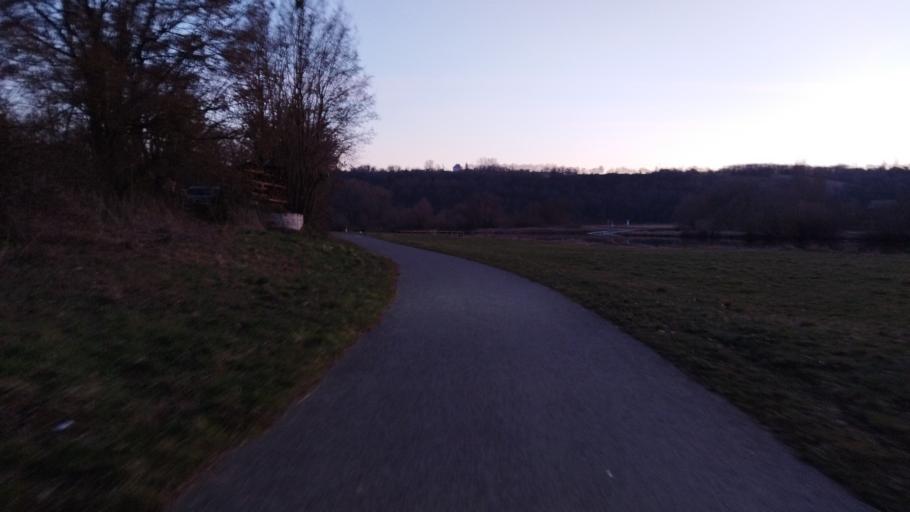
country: DE
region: Bavaria
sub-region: Regierungsbezirk Unterfranken
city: Nordheim
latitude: 49.8771
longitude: 10.1640
